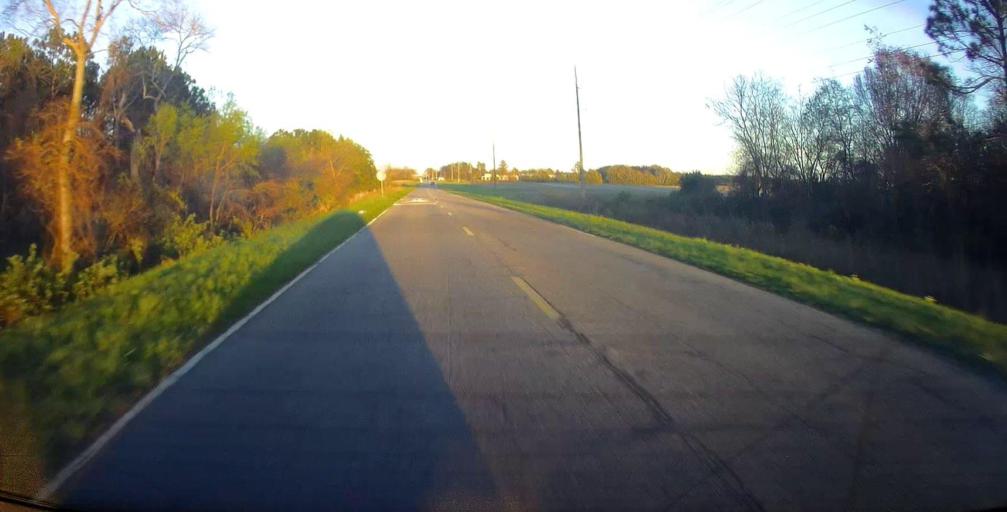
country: US
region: Georgia
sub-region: Crisp County
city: Cordele
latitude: 31.9553
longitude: -83.8037
